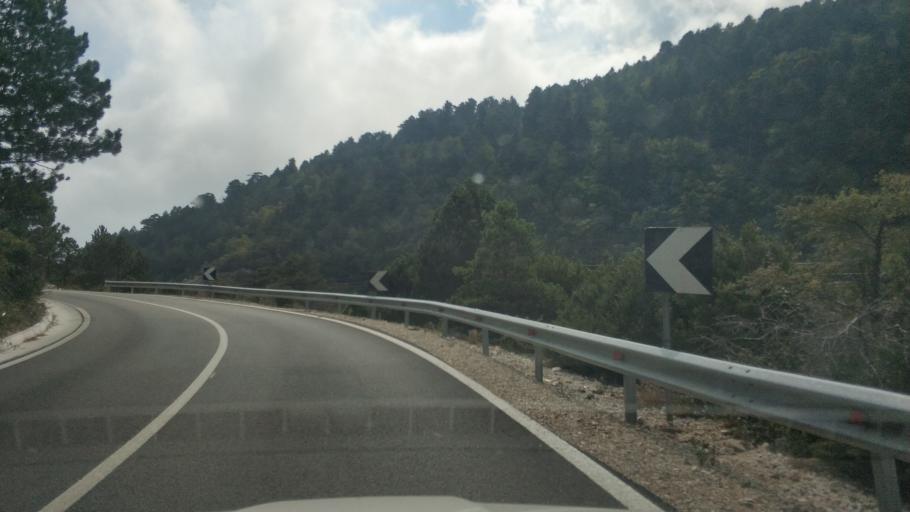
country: AL
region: Vlore
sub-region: Rrethi i Vlores
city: Vranisht
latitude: 40.2007
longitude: 19.5900
